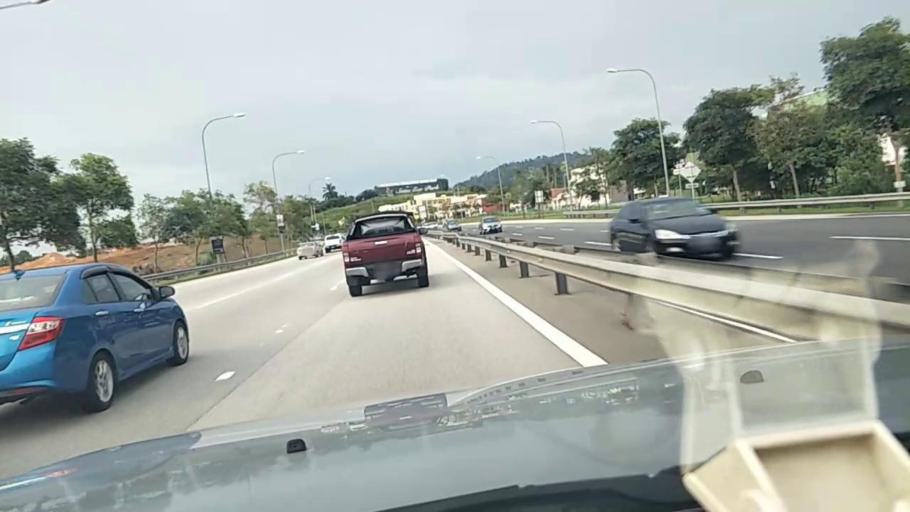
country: MY
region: Selangor
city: Shah Alam
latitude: 3.0951
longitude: 101.4824
